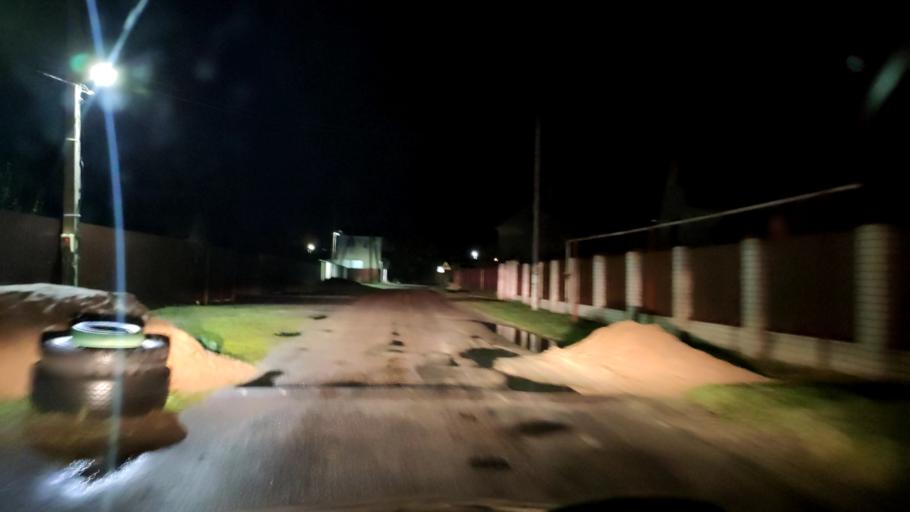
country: RU
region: Voronezj
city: Novaya Usman'
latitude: 51.6098
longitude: 39.4080
